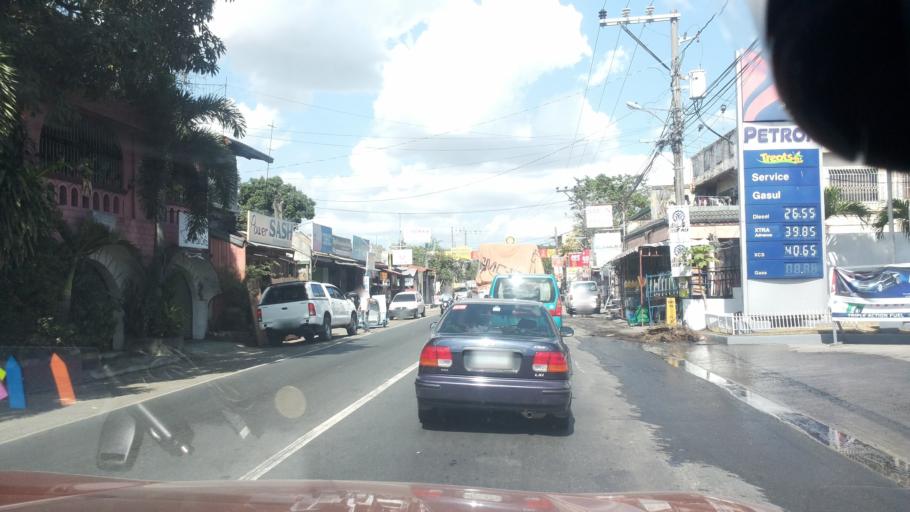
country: PH
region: Central Luzon
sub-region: Province of Bulacan
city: Plaridel
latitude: 14.8665
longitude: 120.8602
